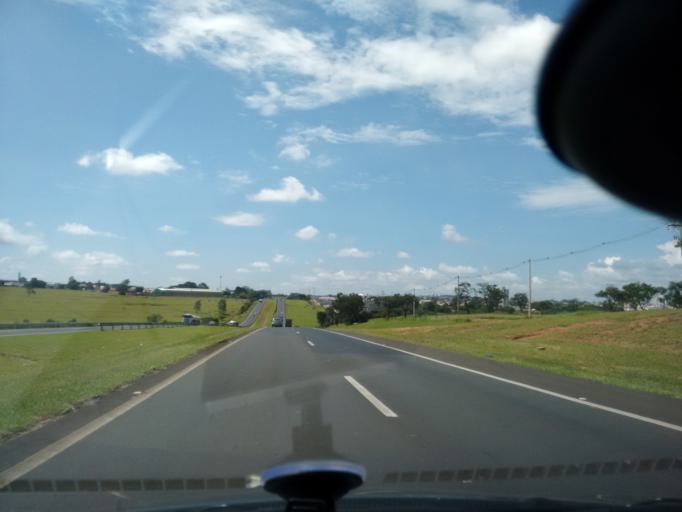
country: BR
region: Sao Paulo
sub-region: Sao Carlos
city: Sao Carlos
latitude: -21.9839
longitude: -47.9087
